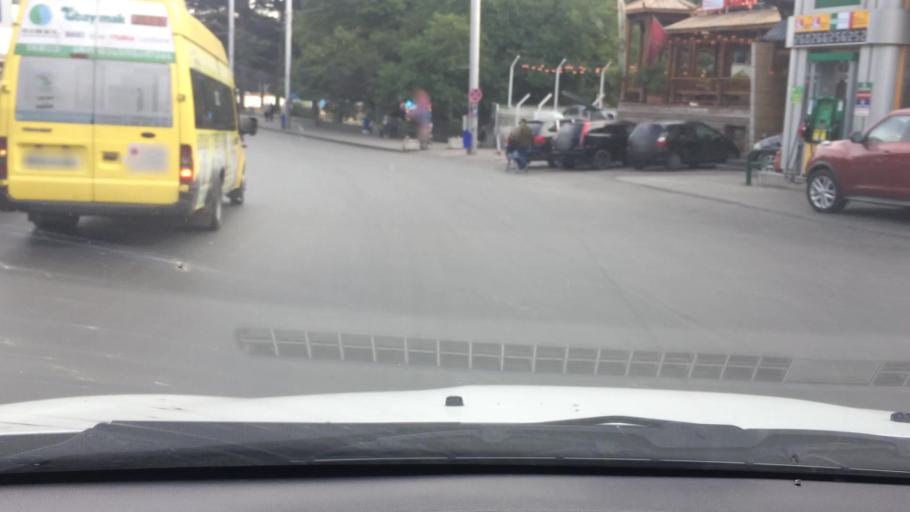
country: GE
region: T'bilisi
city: Tbilisi
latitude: 41.7141
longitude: 44.7799
